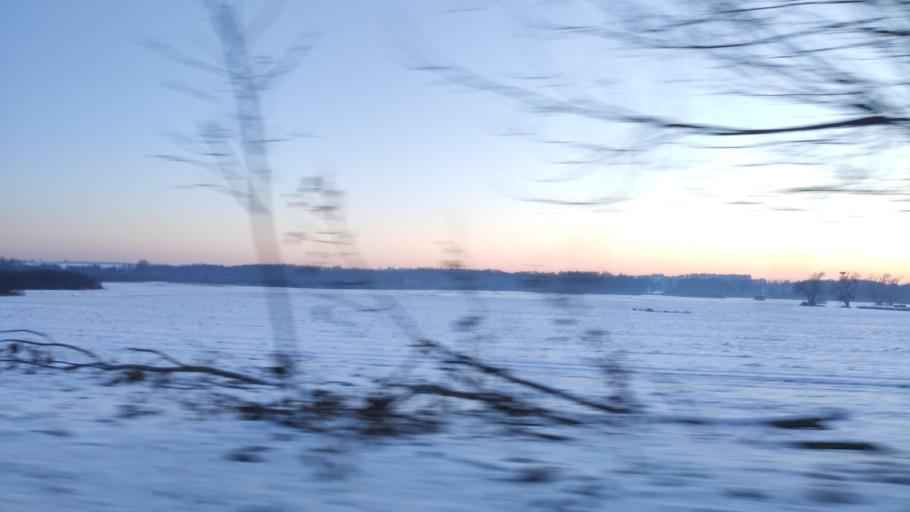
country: PL
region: Kujawsko-Pomorskie
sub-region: Powiat zninski
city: Barcin
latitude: 52.8669
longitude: 17.9136
